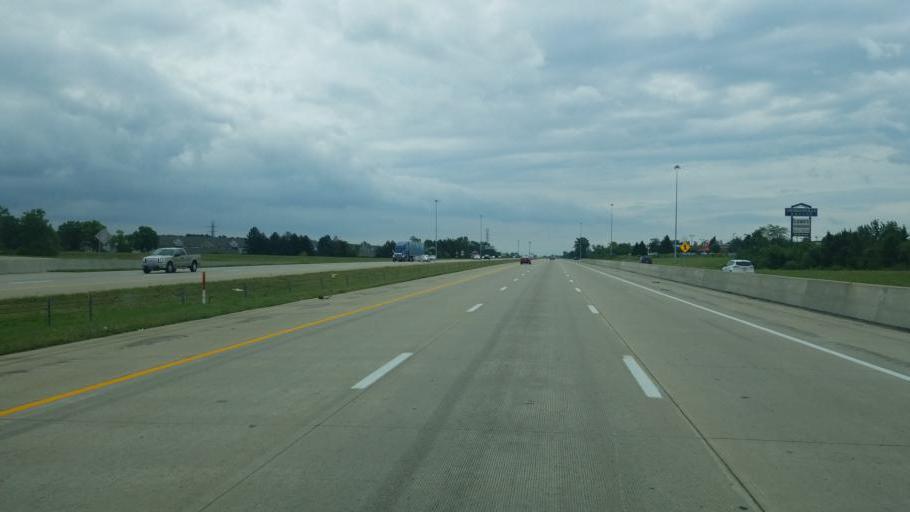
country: US
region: Ohio
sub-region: Franklin County
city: Lincoln Village
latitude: 39.9232
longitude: -83.1197
